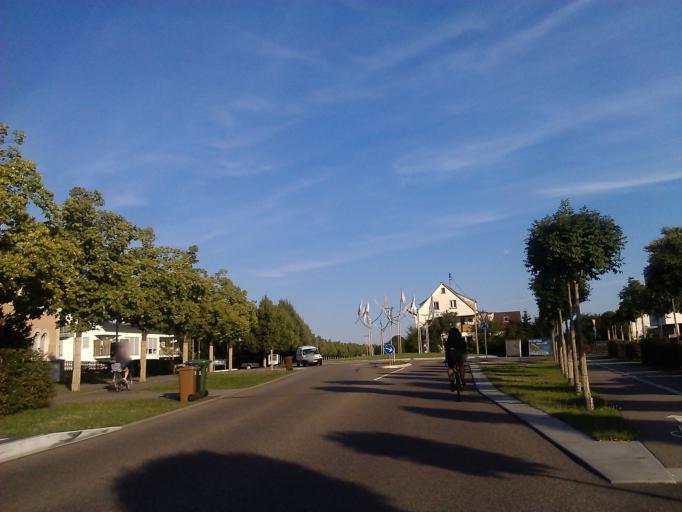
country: DE
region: Baden-Wuerttemberg
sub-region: Karlsruhe Region
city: Walldorf
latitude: 49.3000
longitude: 8.6457
